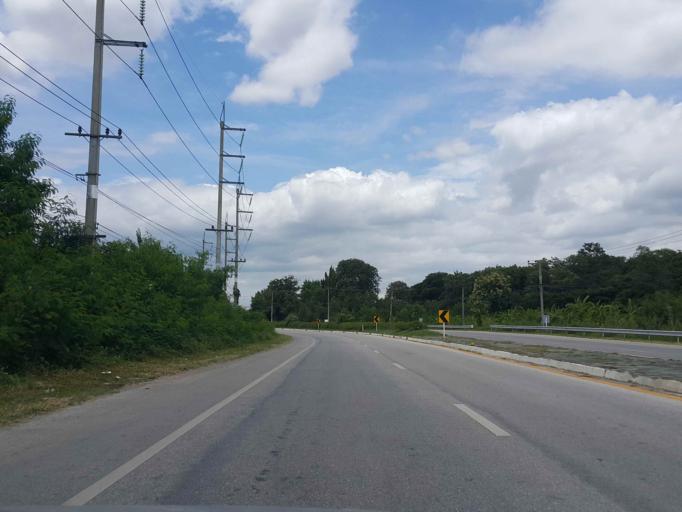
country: TH
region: Lamphun
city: Ban Hong
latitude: 18.3134
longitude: 98.8241
